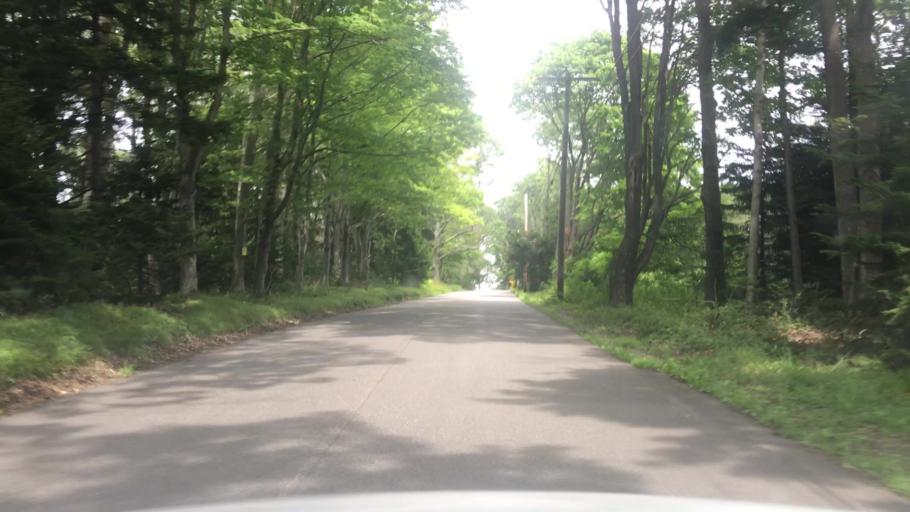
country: US
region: Maine
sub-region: Cumberland County
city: Scarborough
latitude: 43.5637
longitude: -70.2622
